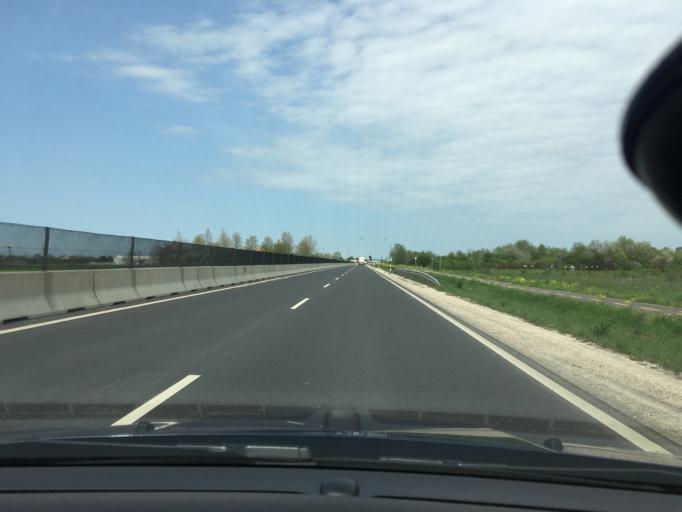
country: HU
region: Csongrad
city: Algyo
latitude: 46.3045
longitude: 20.1820
